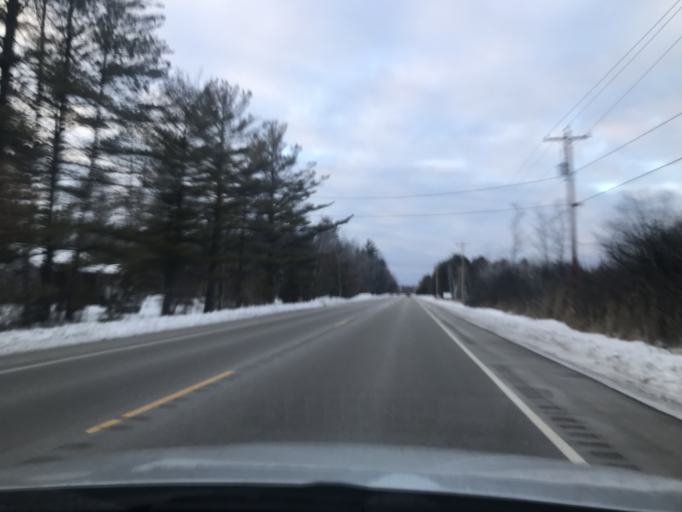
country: US
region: Wisconsin
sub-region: Marinette County
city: Marinette
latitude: 45.1310
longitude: -87.6873
